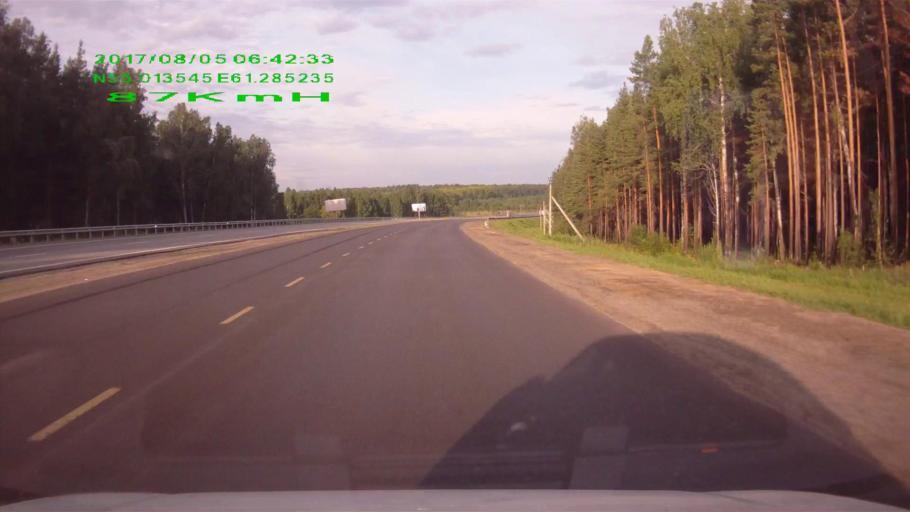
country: RU
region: Chelyabinsk
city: Sargazy
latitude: 55.0133
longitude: 61.2846
